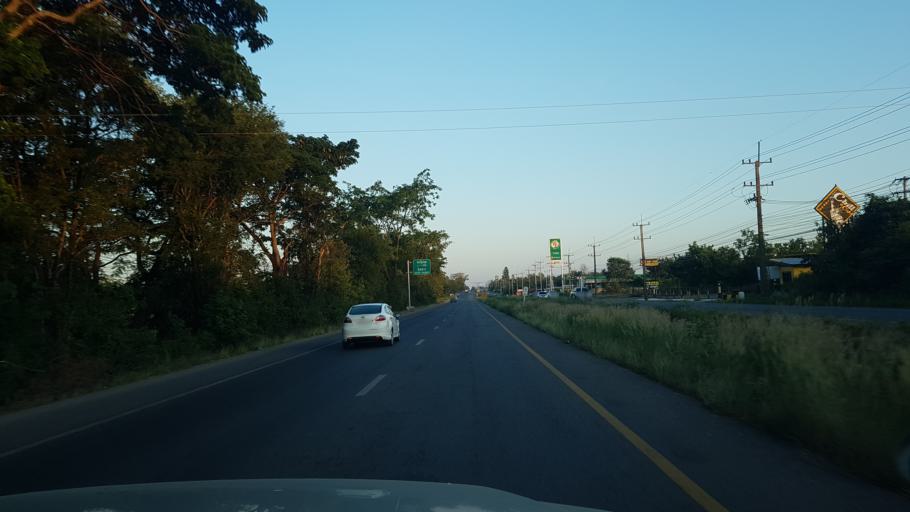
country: TH
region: Khon Kaen
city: Chum Phae
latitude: 16.5794
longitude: 102.0215
